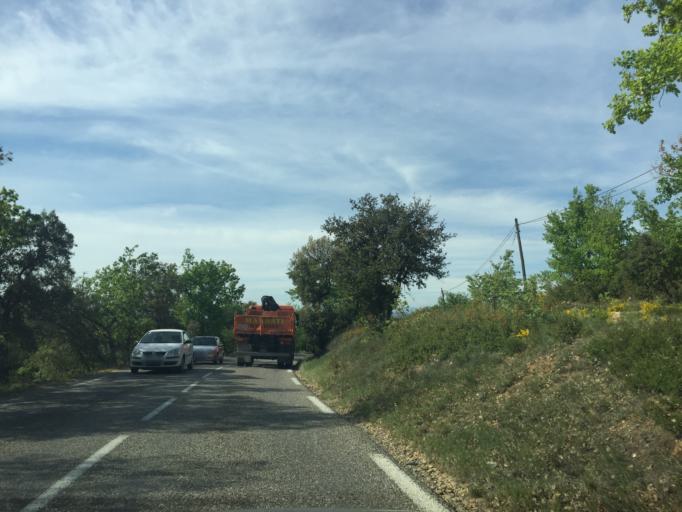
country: FR
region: Provence-Alpes-Cote d'Azur
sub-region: Departement du Var
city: Vinon-sur-Verdon
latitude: 43.7118
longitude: 5.8151
